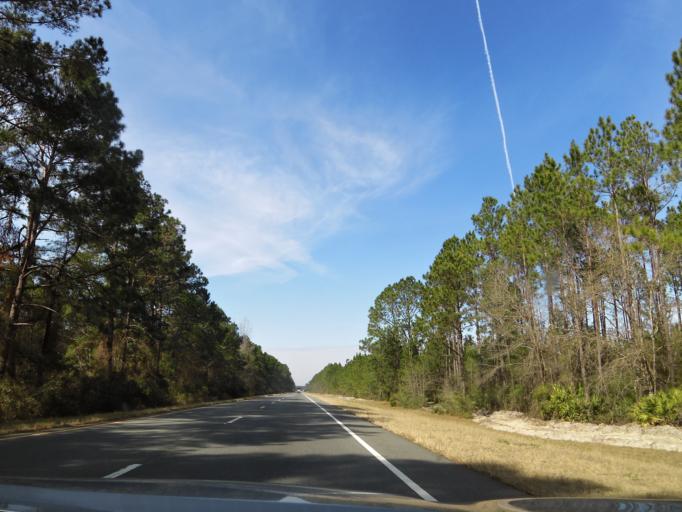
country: US
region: Georgia
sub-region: Ware County
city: Waycross
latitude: 31.1125
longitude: -82.2457
